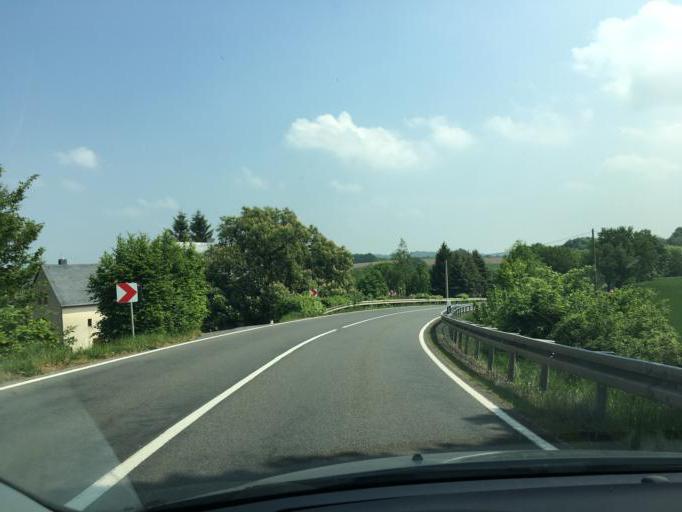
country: DE
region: Saxony
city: Colditz
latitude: 51.1444
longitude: 12.7738
